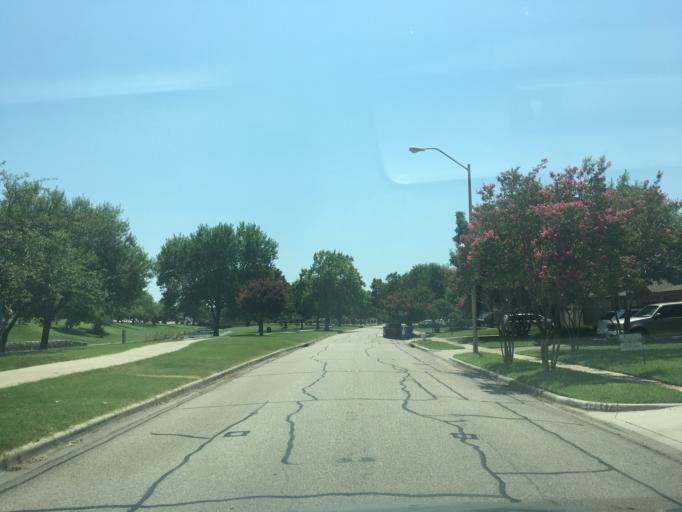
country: US
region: Texas
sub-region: Dallas County
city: Farmers Branch
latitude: 32.9299
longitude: -96.8798
